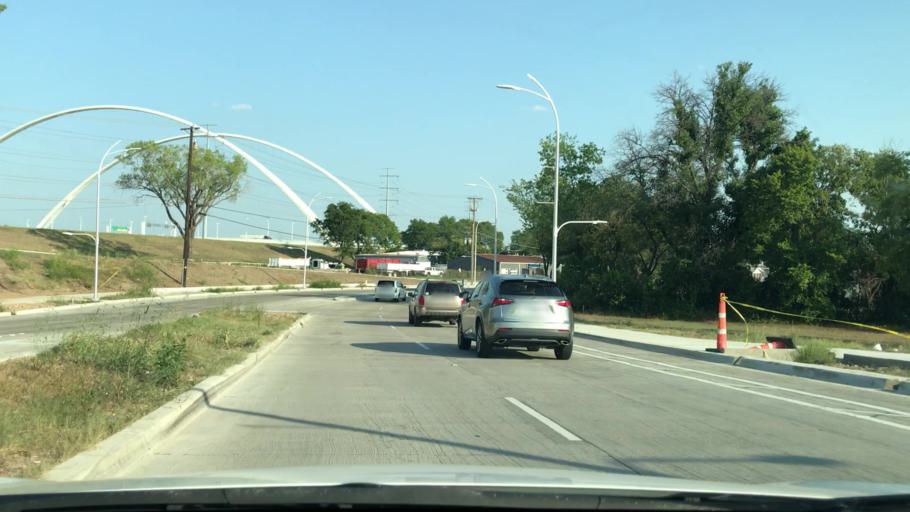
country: US
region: Texas
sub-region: Dallas County
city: Dallas
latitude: 32.7742
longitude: -96.8234
